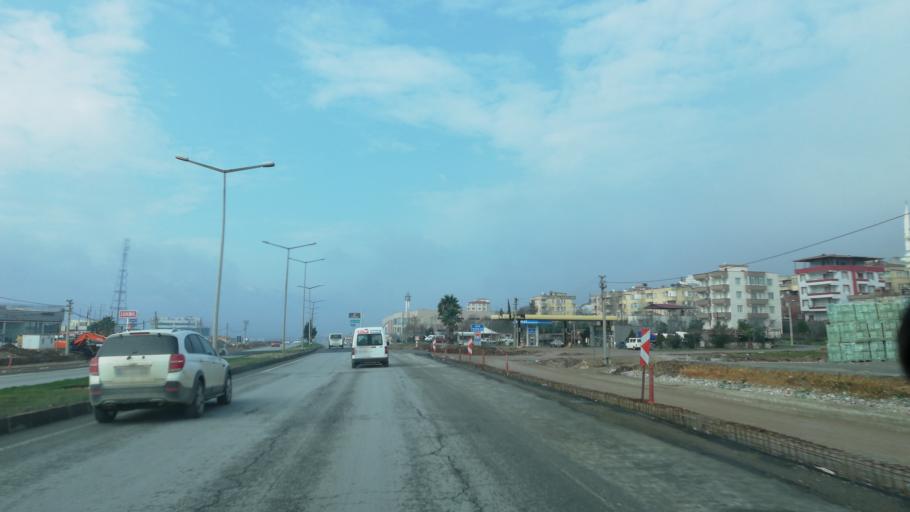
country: TR
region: Kahramanmaras
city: Kahramanmaras
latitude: 37.5691
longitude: 36.9142
